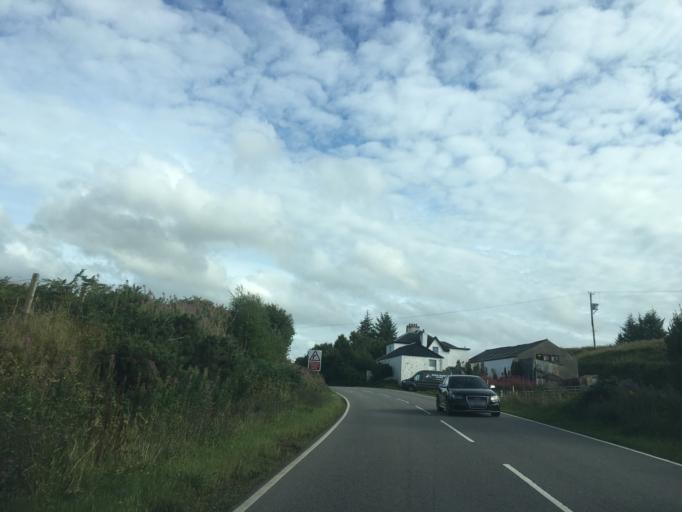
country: GB
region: Scotland
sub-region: Argyll and Bute
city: Oban
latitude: 56.3904
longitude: -5.4601
